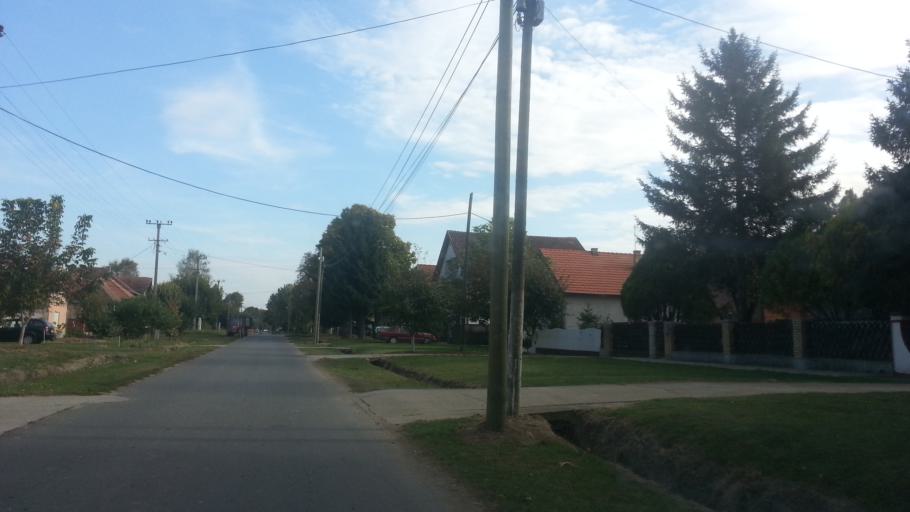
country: RS
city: Belegis
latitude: 45.0211
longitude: 20.3159
